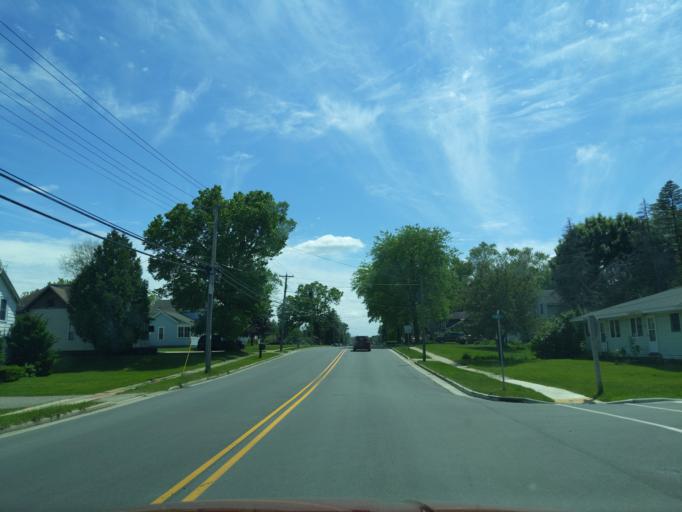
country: US
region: Wisconsin
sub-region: Columbia County
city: Pardeeville
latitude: 43.5321
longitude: -89.3017
